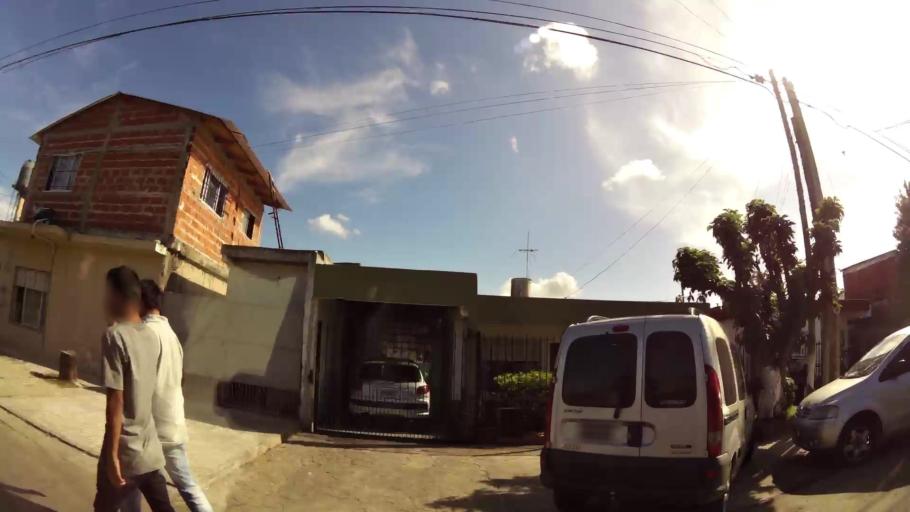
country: AR
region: Buenos Aires
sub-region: Partido de Quilmes
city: Quilmes
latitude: -34.7958
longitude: -58.2405
